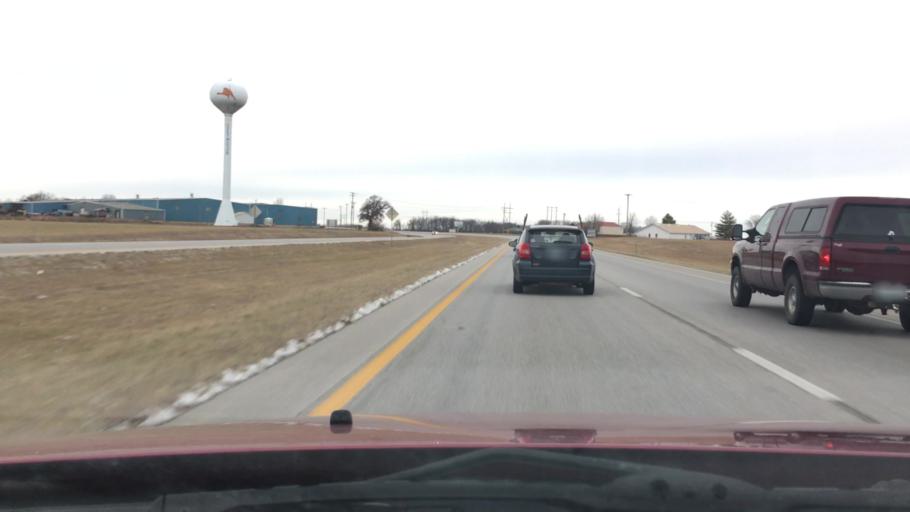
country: US
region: Missouri
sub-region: Webster County
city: Seymour
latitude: 37.1521
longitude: -92.7556
